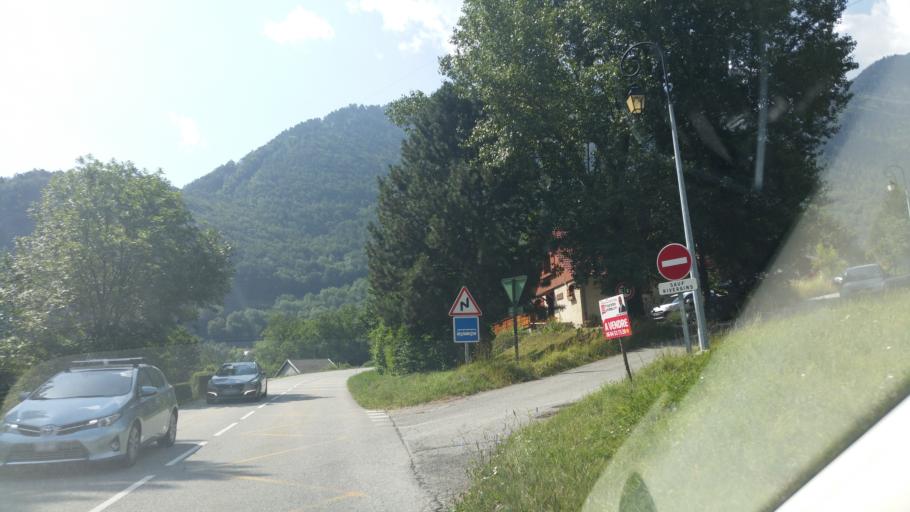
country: FR
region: Rhone-Alpes
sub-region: Departement de la Savoie
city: Aigueblanche
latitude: 45.4991
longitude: 6.5051
